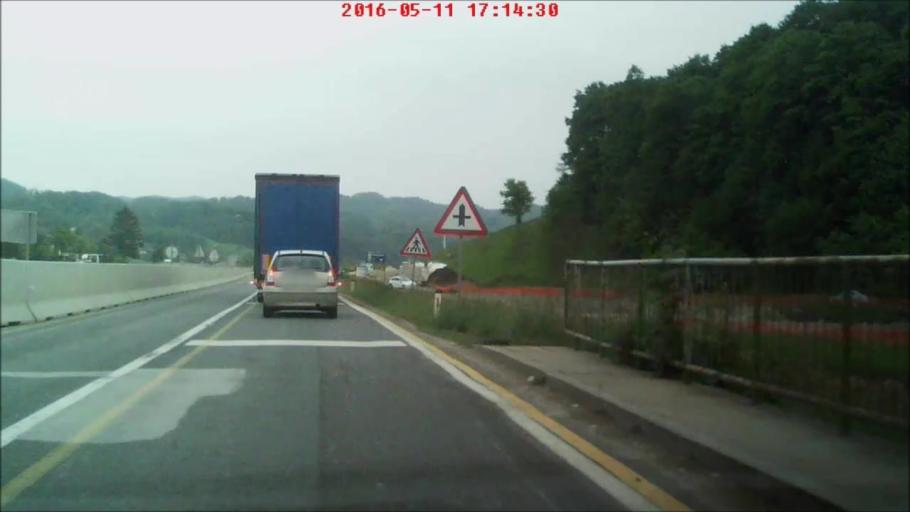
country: SI
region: Podlehnik
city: Podlehnik
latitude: 46.3330
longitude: 15.8768
